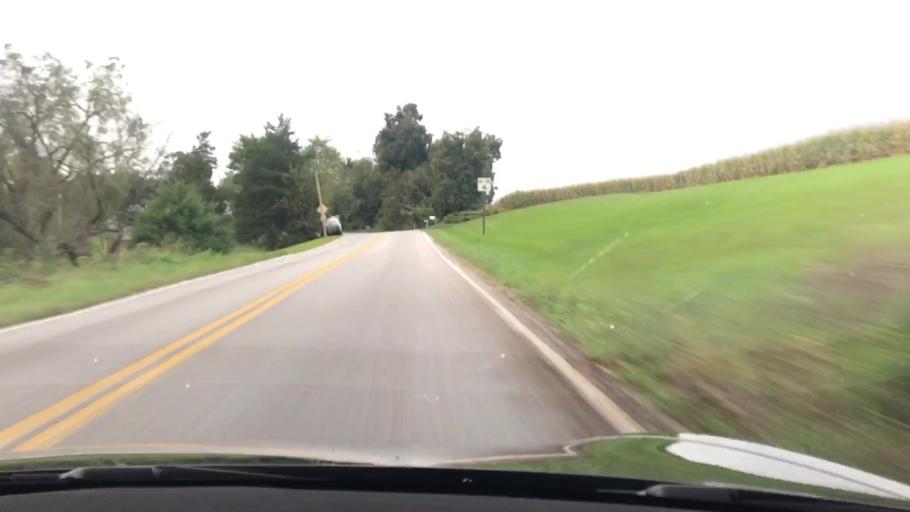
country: US
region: Pennsylvania
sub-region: York County
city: Weigelstown
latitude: 39.9484
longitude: -76.8619
